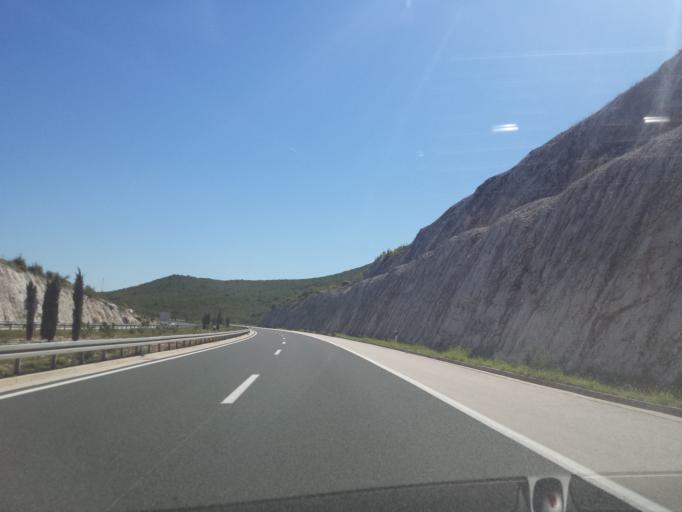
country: HR
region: Splitsko-Dalmatinska
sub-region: Grad Omis
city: Omis
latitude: 43.4798
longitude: 16.8088
